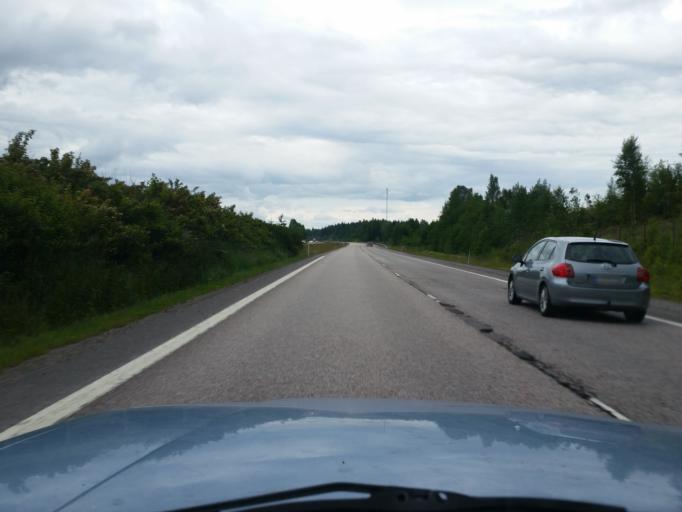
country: FI
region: Uusimaa
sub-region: Helsinki
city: Maentsaelae
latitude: 60.7081
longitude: 25.4171
